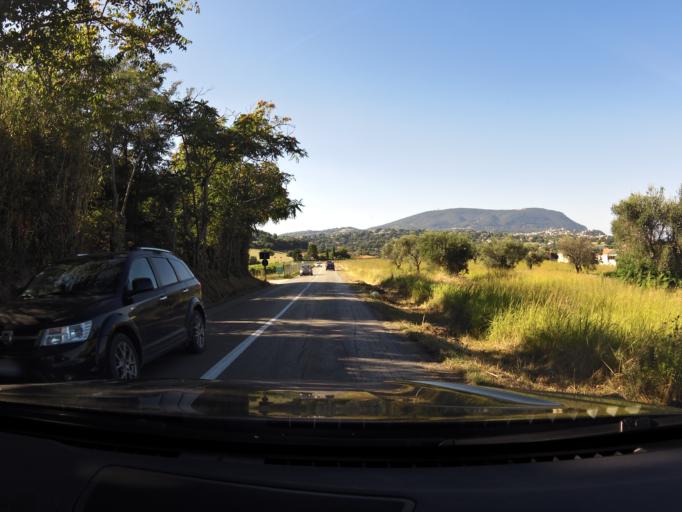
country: IT
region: The Marches
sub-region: Provincia di Ancona
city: Marcelli
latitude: 43.4896
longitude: 13.6168
